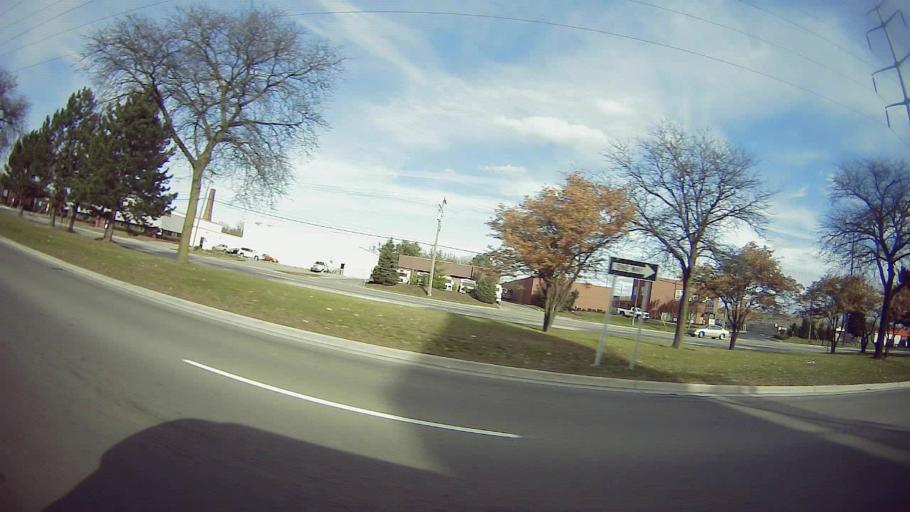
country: US
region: Michigan
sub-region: Oakland County
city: Southfield
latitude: 42.4438
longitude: -83.2358
